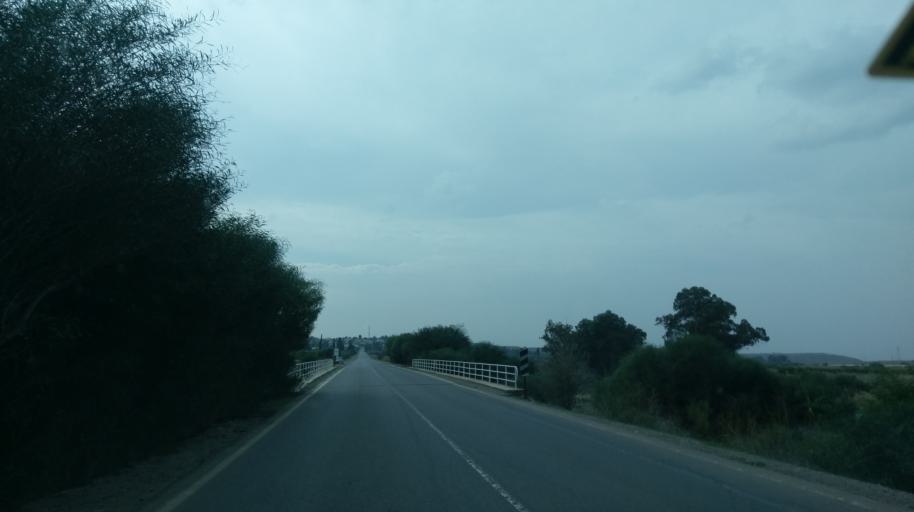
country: CY
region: Lefkosia
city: Akaki
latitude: 35.1935
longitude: 33.1064
